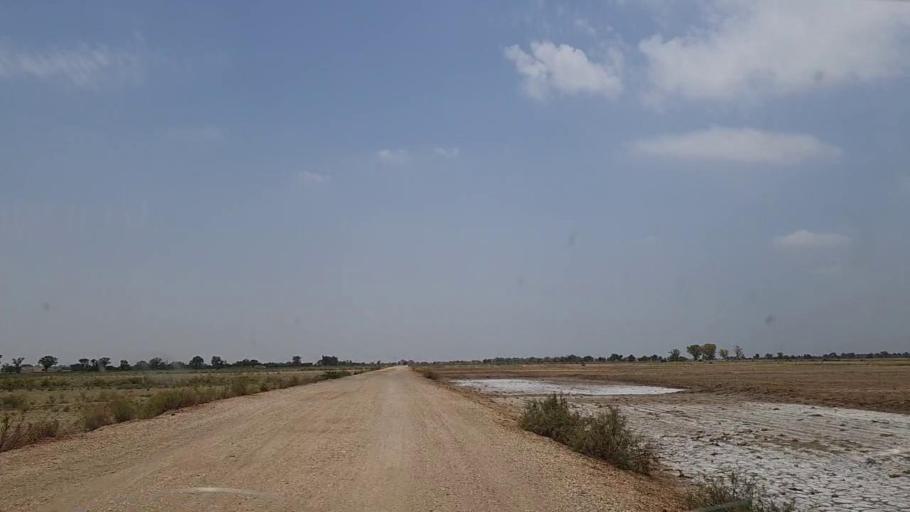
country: PK
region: Sindh
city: Phulji
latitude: 26.8119
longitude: 67.6340
